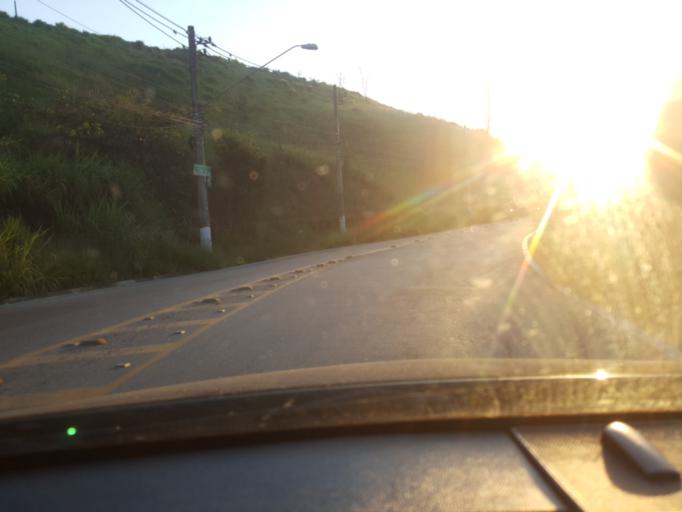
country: BR
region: Sao Paulo
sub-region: Cajamar
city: Cajamar
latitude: -23.3951
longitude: -46.8654
